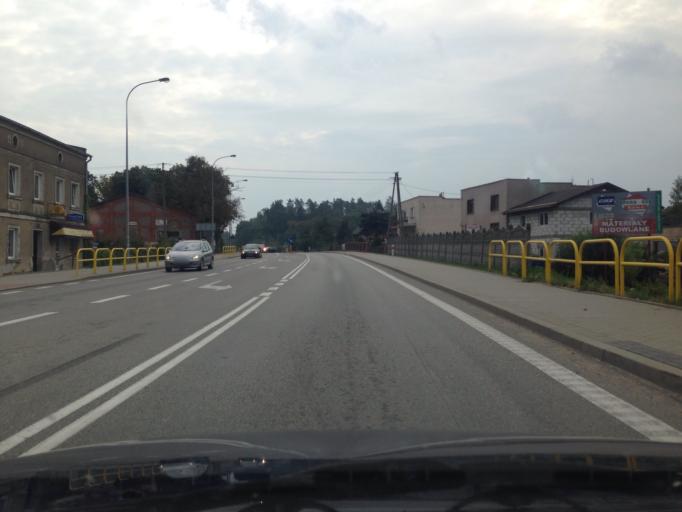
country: PL
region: Pomeranian Voivodeship
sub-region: Powiat starogardzki
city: Smetowo Graniczne
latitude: 53.7331
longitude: 18.7339
